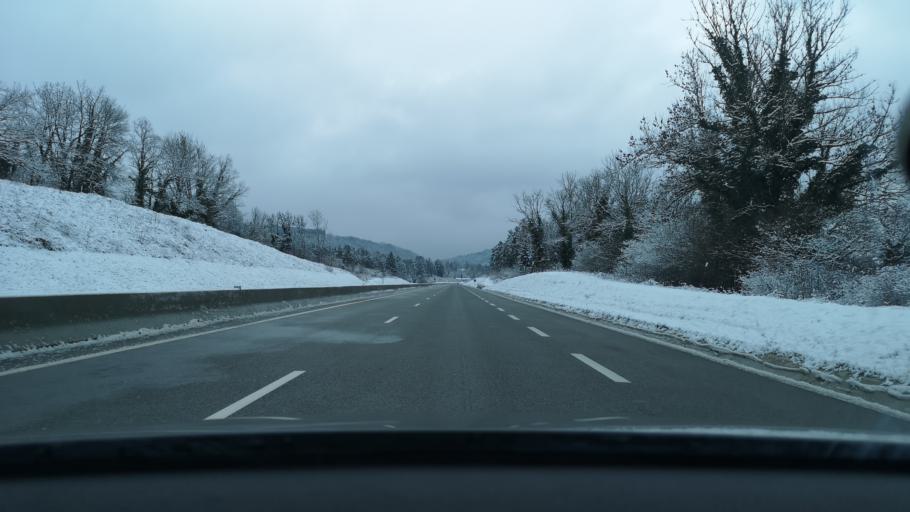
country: FR
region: Rhone-Alpes
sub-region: Departement de l'Ain
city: Dortan
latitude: 46.3157
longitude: 5.6703
